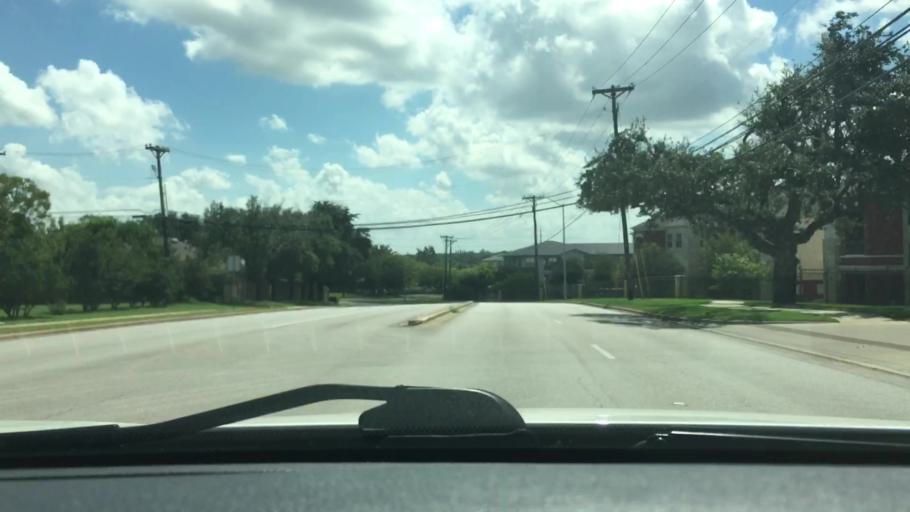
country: US
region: Texas
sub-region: Williamson County
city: Round Rock
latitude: 30.5431
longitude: -97.6732
